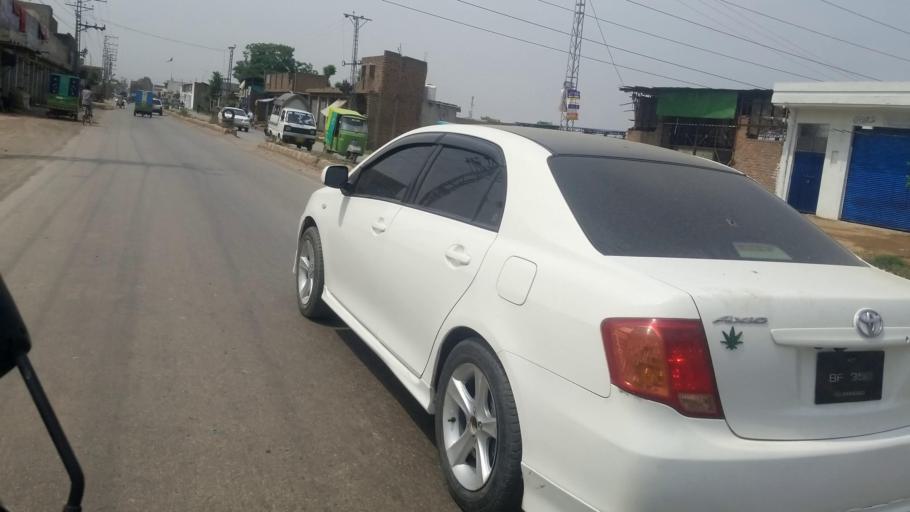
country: PK
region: Khyber Pakhtunkhwa
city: Peshawar
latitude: 33.9945
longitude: 71.6115
